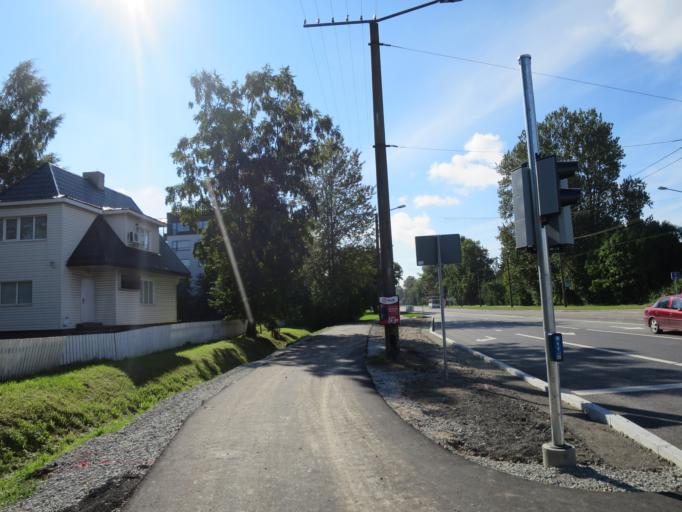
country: EE
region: Harju
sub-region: Tallinna linn
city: Tallinn
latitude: 59.4227
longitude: 24.7159
